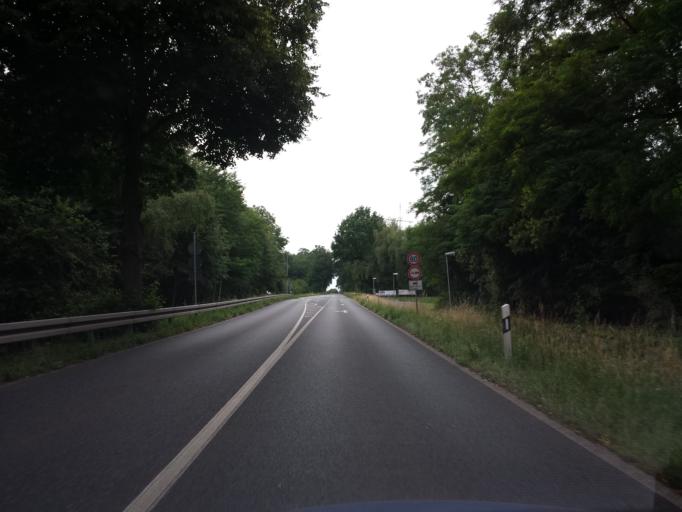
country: DE
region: Hesse
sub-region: Regierungsbezirk Darmstadt
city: Dietzenbach
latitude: 49.9765
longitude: 8.7749
